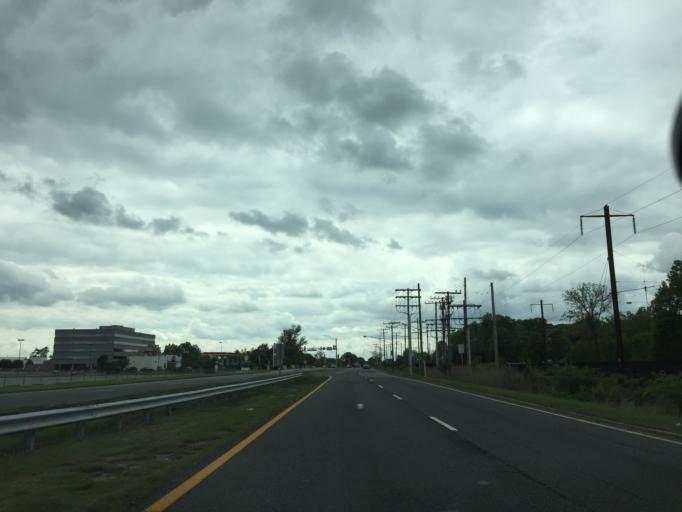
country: US
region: Maryland
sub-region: Baltimore County
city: Middle River
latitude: 39.3346
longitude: -76.4313
